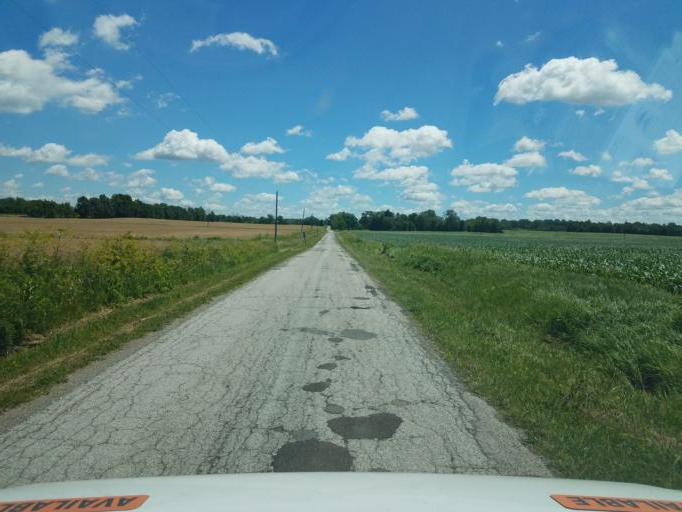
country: US
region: Ohio
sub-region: Crawford County
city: Galion
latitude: 40.7125
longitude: -82.8527
